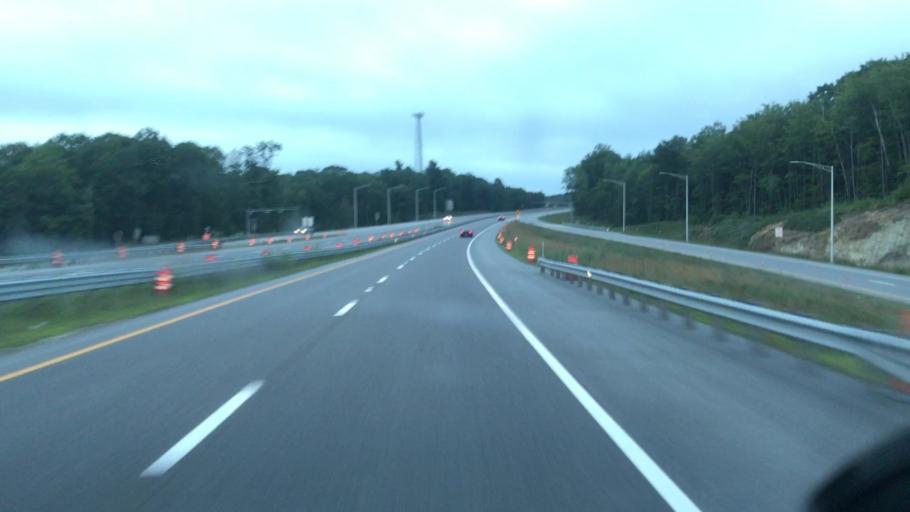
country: US
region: Maine
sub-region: Androscoggin County
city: Lewiston
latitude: 44.0721
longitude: -70.1840
